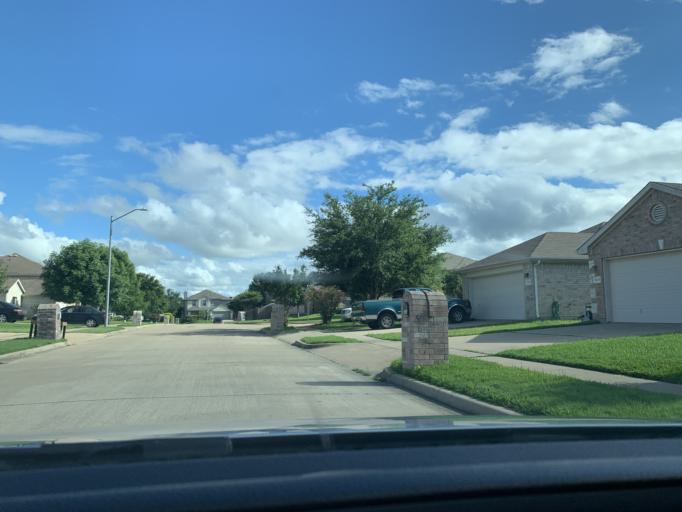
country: US
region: Texas
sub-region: Dallas County
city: Cedar Hill
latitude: 32.6419
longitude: -97.0334
